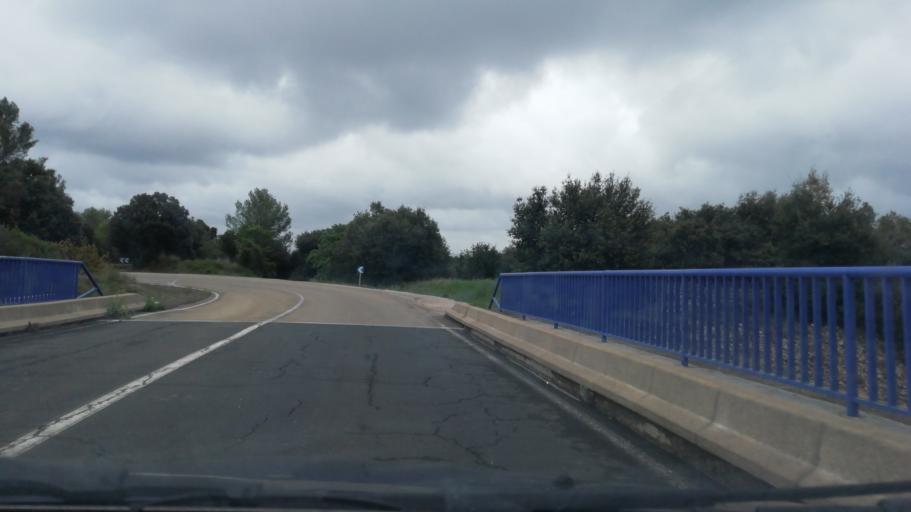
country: FR
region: Languedoc-Roussillon
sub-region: Departement de l'Herault
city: Saint-Gely-du-Fesc
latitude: 43.7101
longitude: 3.7993
